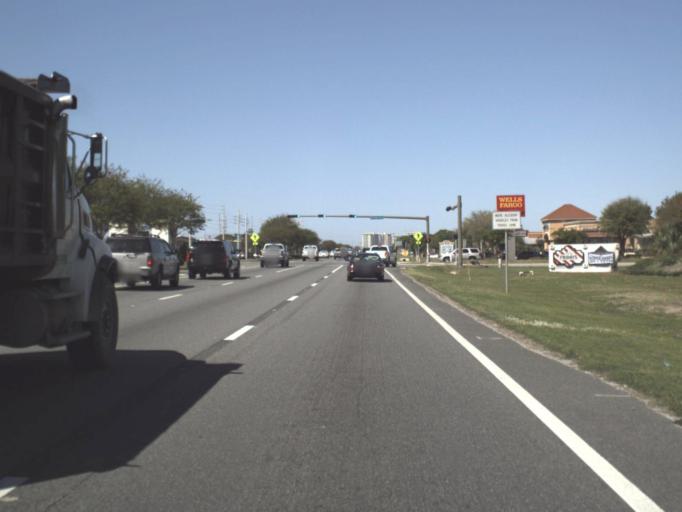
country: US
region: Florida
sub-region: Okaloosa County
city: Destin
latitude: 30.3885
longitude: -86.4293
